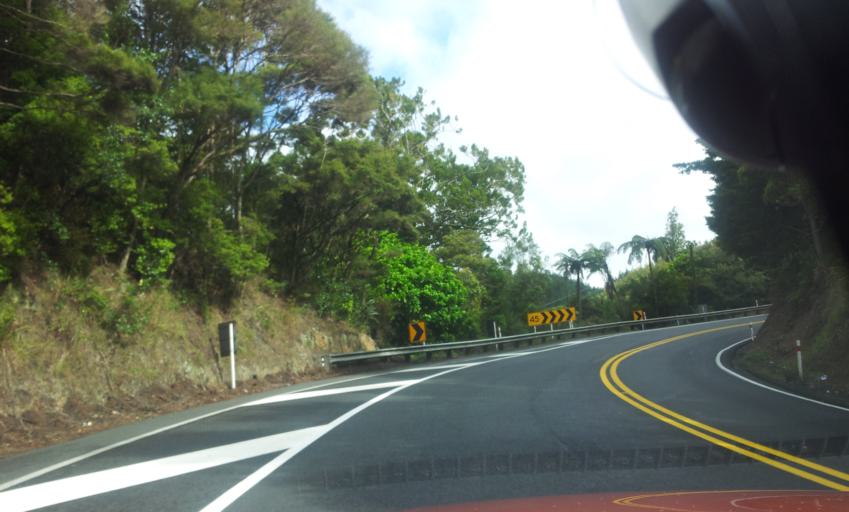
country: NZ
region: Northland
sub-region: Whangarei
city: Ruakaka
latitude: -36.0757
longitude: 174.4200
